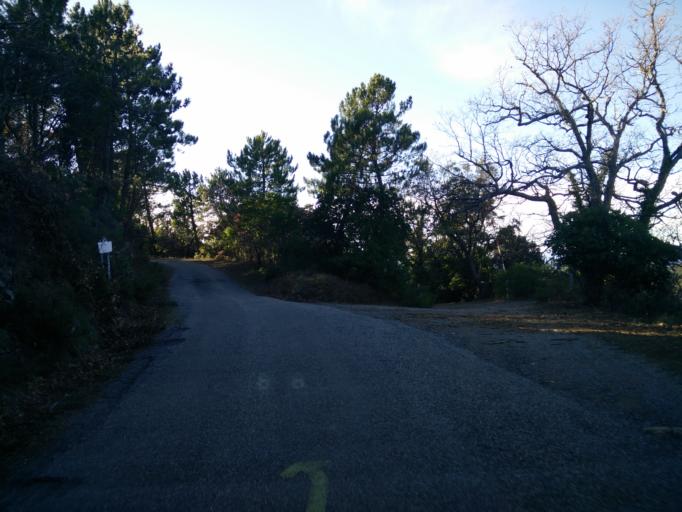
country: FR
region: Provence-Alpes-Cote d'Azur
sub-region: Departement du Var
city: Collobrieres
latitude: 43.2689
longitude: 6.2920
